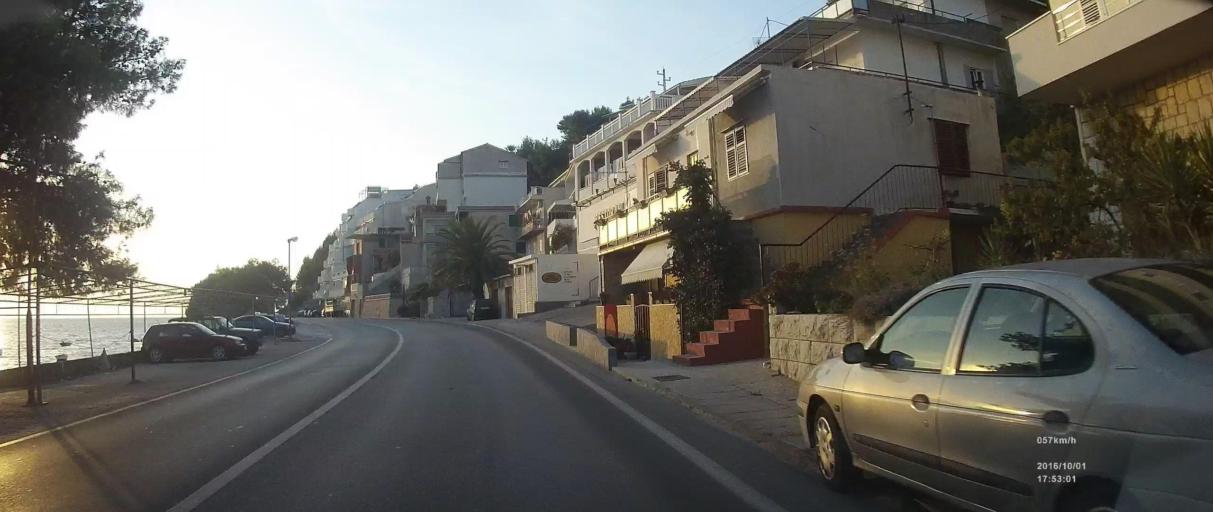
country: HR
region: Splitsko-Dalmatinska
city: Jesenice
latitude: 43.4566
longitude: 16.6146
